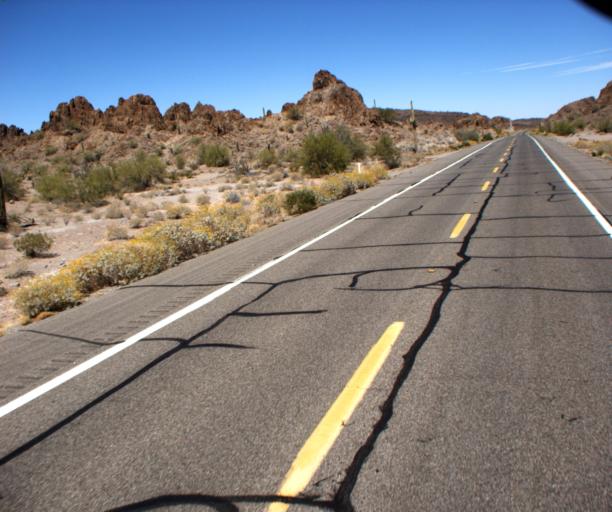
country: US
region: Arizona
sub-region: Pima County
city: Ajo
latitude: 32.5448
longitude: -112.8800
